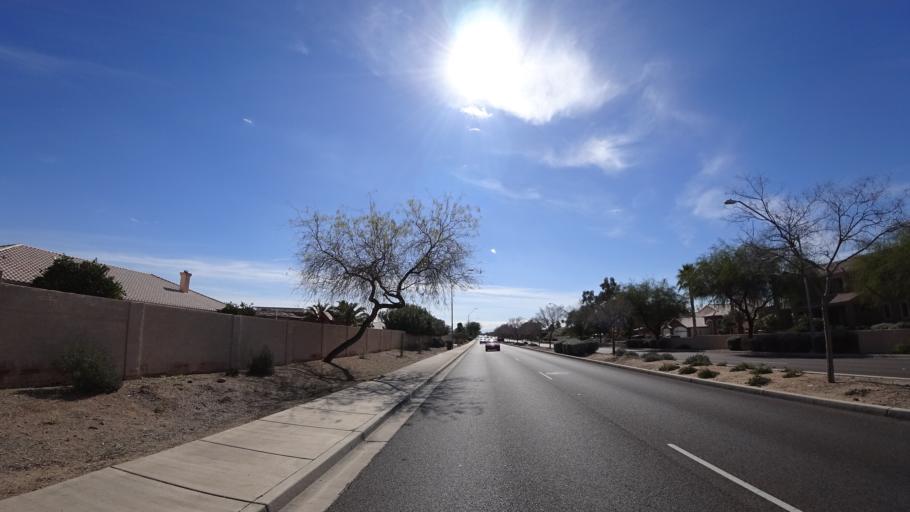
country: US
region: Arizona
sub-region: Maricopa County
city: Peoria
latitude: 33.6479
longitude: -112.2029
